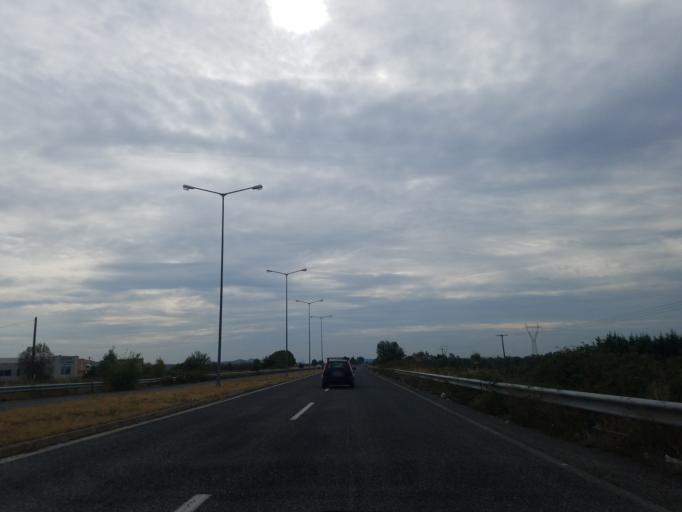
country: GR
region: Thessaly
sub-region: Trikala
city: Vasiliki
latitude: 39.6288
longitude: 21.7048
